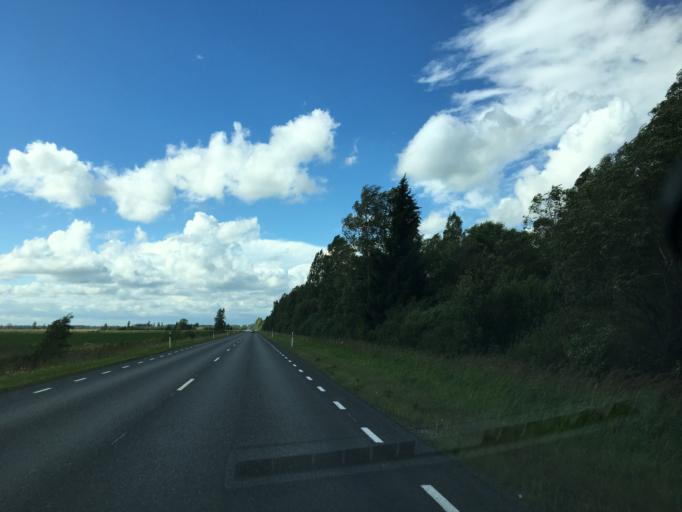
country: EE
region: Paernumaa
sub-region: Vaendra vald (alev)
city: Vandra
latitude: 58.5908
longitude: 25.1607
